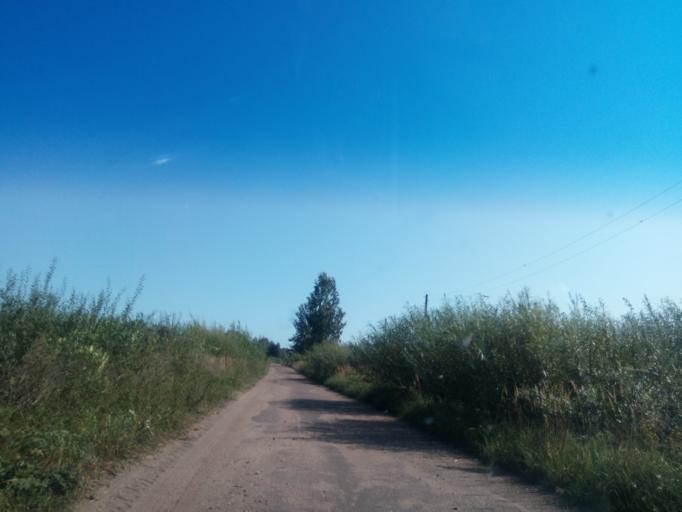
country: BY
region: Vitebsk
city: Dzisna
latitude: 55.6463
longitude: 28.2467
